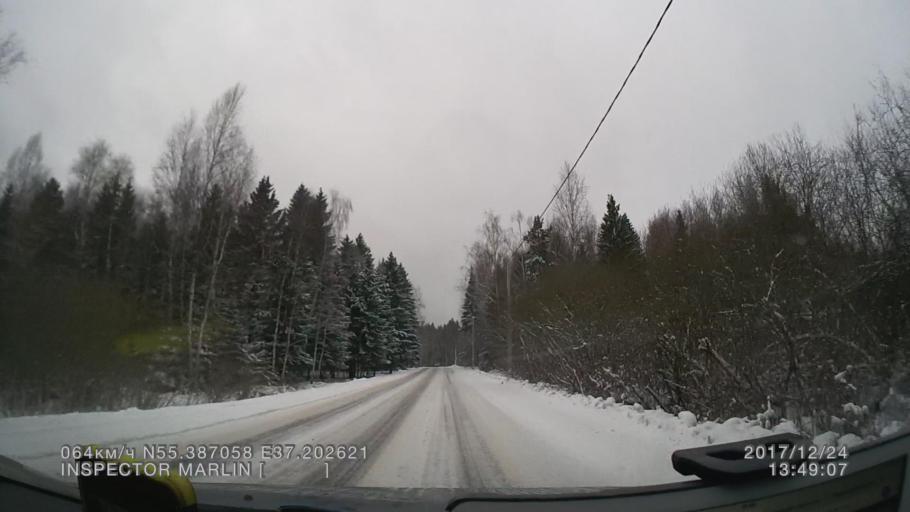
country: RU
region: Moskovskaya
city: Troitsk
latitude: 55.3871
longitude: 37.2025
